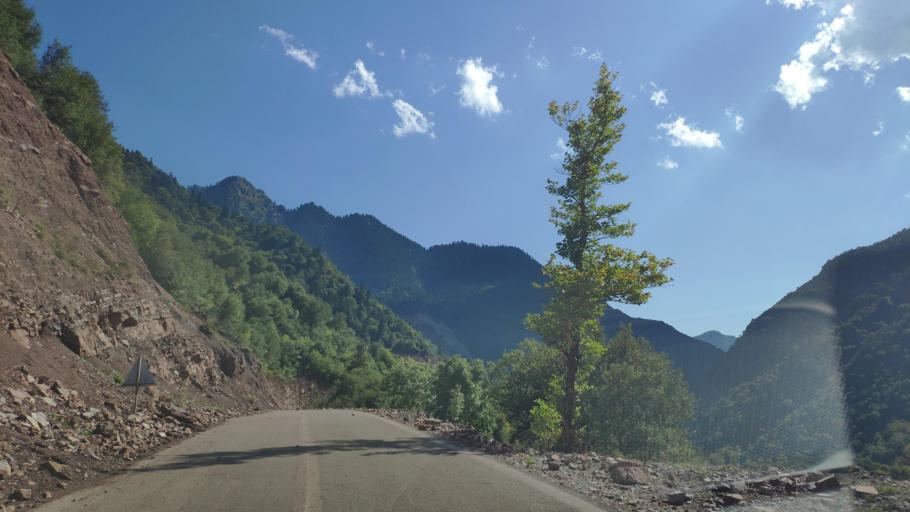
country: GR
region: Central Greece
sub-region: Nomos Evrytanias
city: Kerasochori
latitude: 39.1298
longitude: 21.6269
